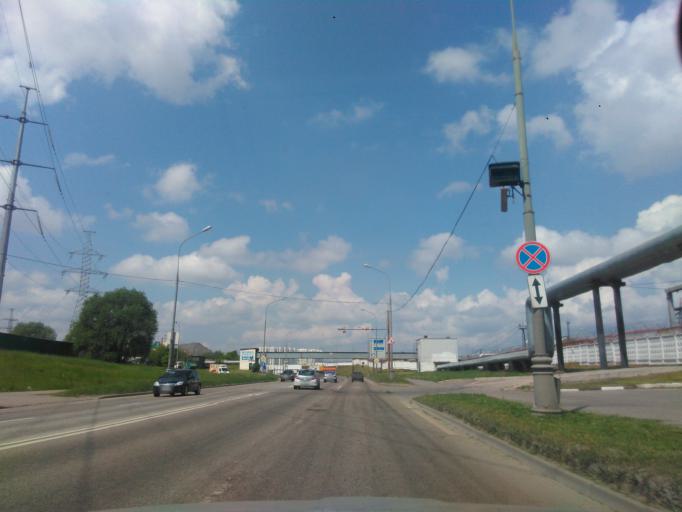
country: RU
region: Moscow
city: Businovo
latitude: 55.8882
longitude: 37.5034
